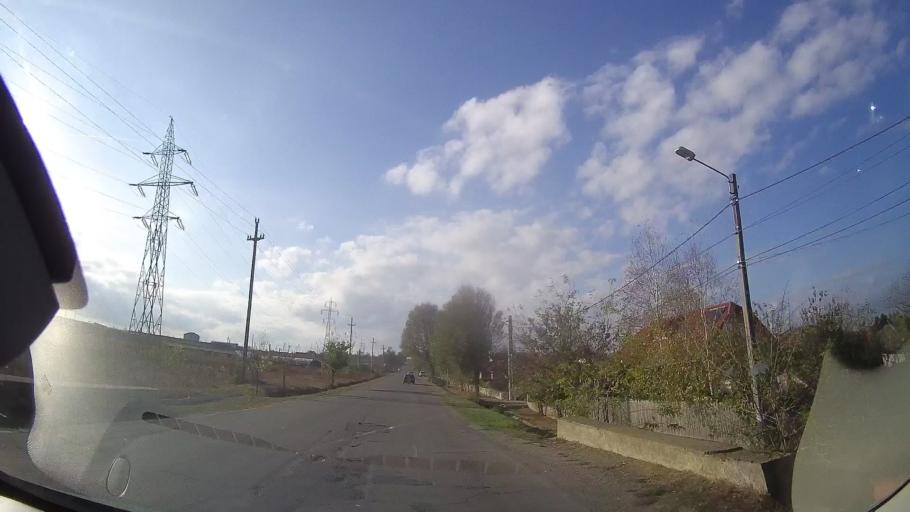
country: RO
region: Constanta
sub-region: Comuna Limanu
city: Limanu
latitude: 43.7939
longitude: 28.5357
